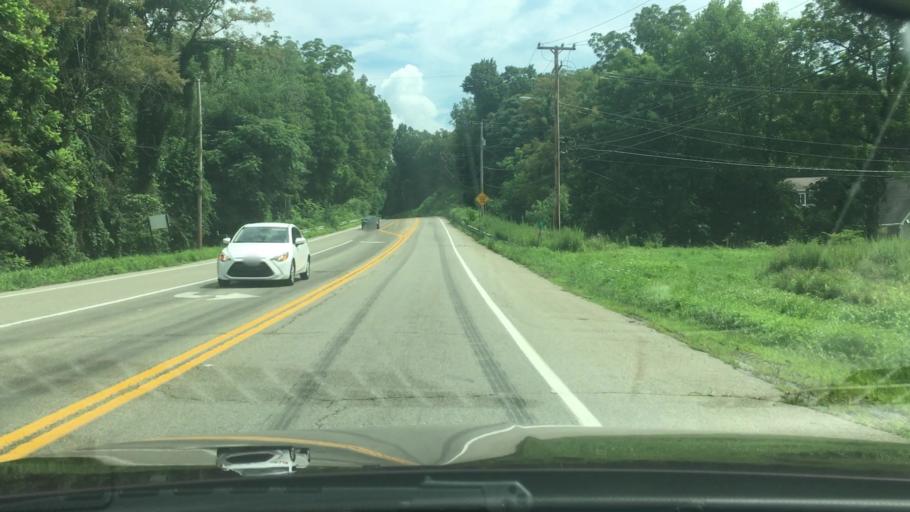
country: US
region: New York
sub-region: Dutchess County
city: Brinckerhoff
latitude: 41.5475
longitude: -73.8183
